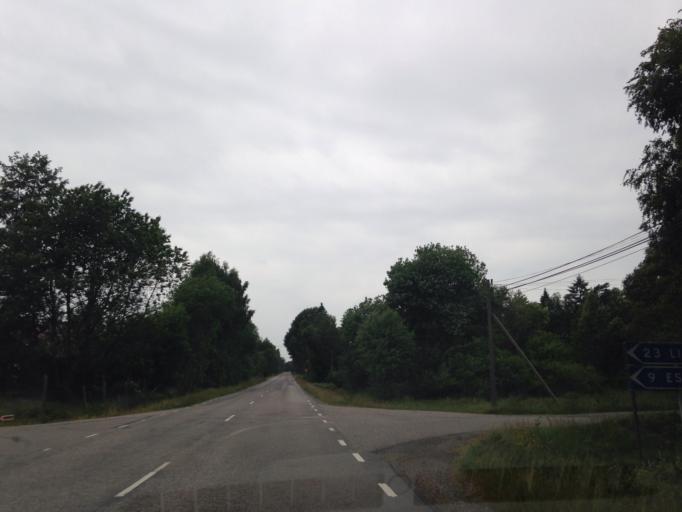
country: SE
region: Vaestra Goetaland
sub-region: Harryda Kommun
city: Hindas
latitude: 57.6729
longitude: 12.3508
